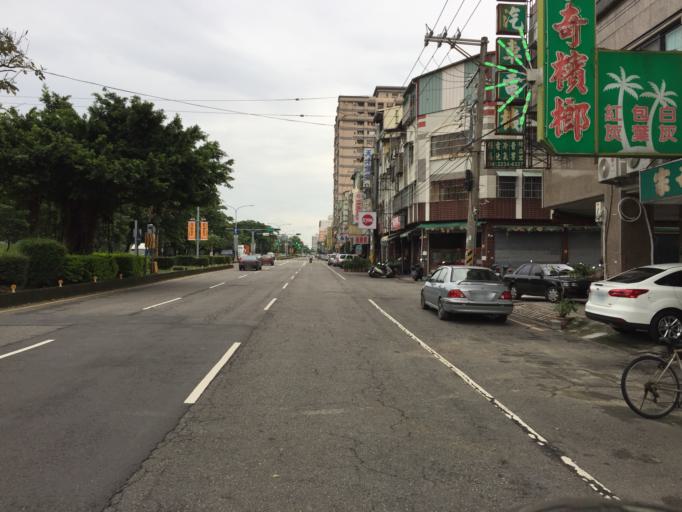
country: TW
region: Taiwan
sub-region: Taichung City
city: Taichung
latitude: 24.1520
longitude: 120.6985
